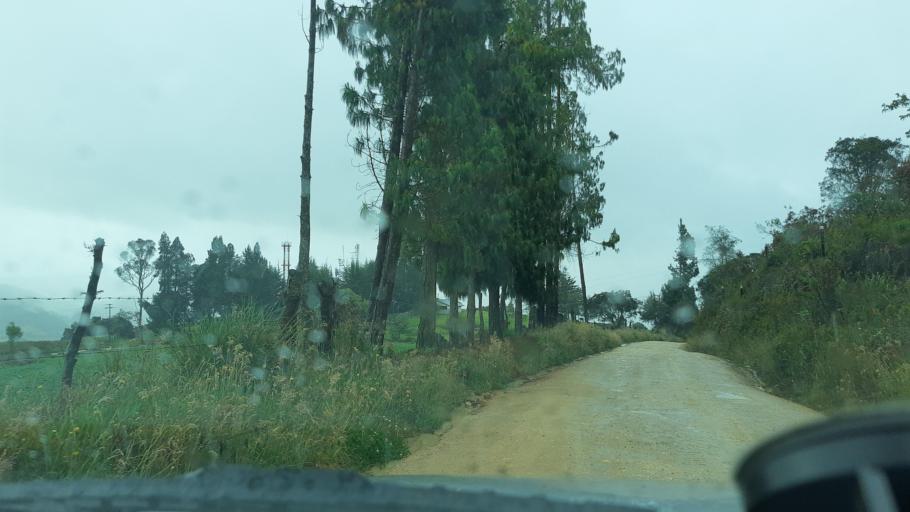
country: CO
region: Cundinamarca
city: Villapinzon
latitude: 5.2115
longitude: -73.5691
